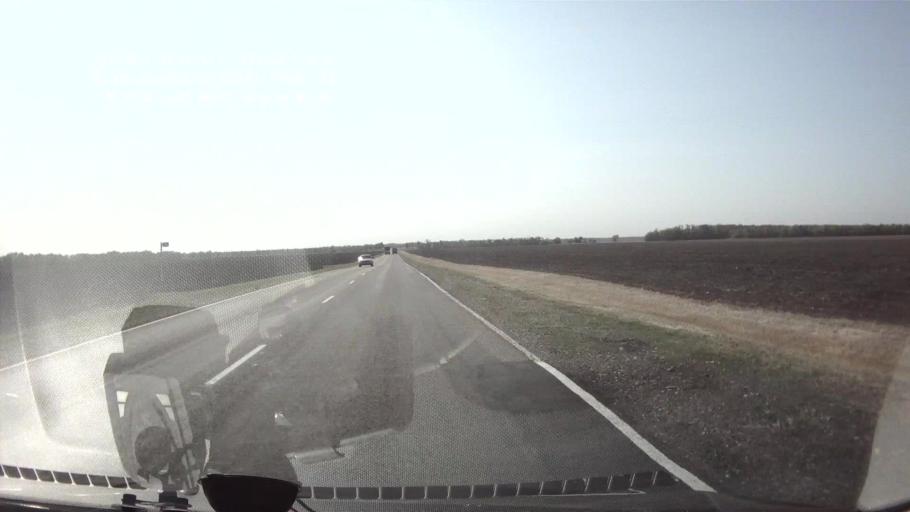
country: RU
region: Krasnodarskiy
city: Belaya Glina
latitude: 46.0285
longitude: 40.7984
